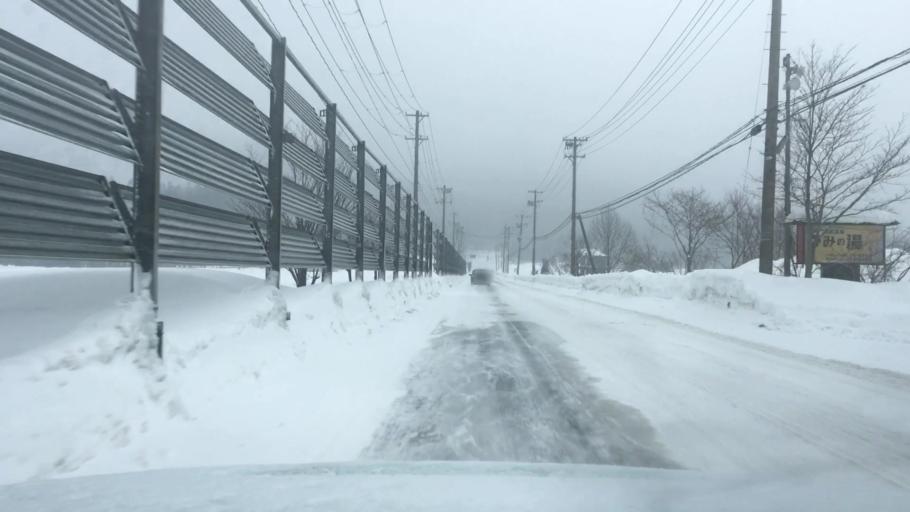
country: JP
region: Akita
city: Hanawa
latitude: 40.0140
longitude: 140.9869
